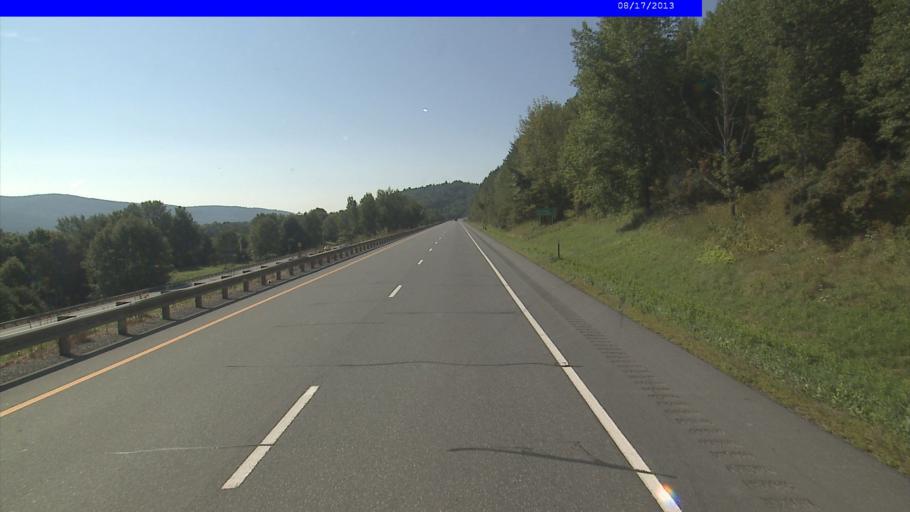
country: US
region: Vermont
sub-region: Windsor County
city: Windsor
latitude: 43.5161
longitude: -72.4084
